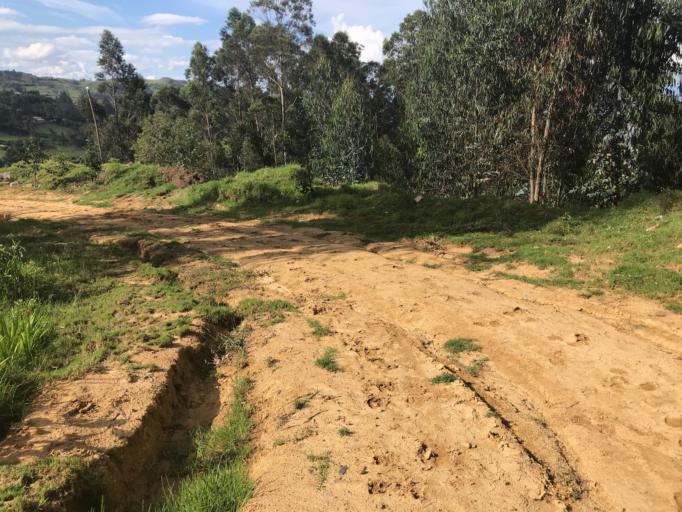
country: PE
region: Cajamarca
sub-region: Provincia de Chota
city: Querocoto
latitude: -6.3632
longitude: -79.0304
